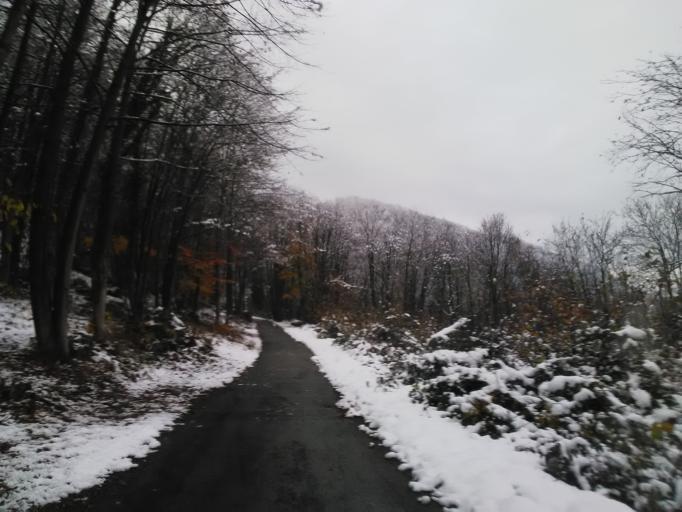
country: IT
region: Piedmont
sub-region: Provincia di Vercelli
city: Varallo
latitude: 45.7907
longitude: 8.2528
